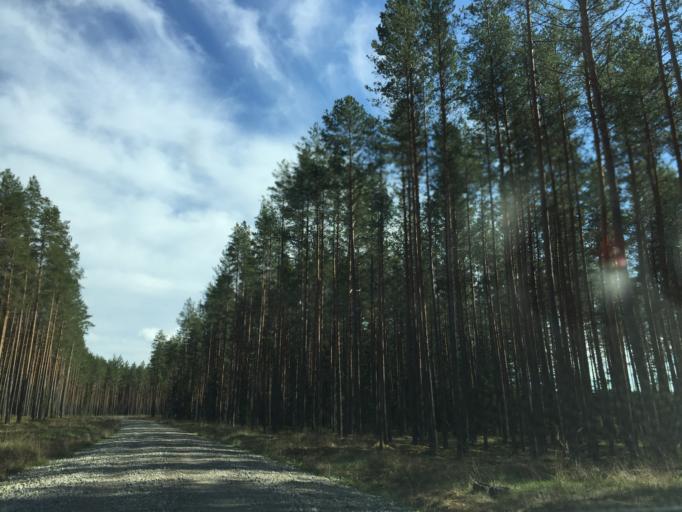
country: LV
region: Strenci
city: Strenci
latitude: 57.5835
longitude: 25.7083
